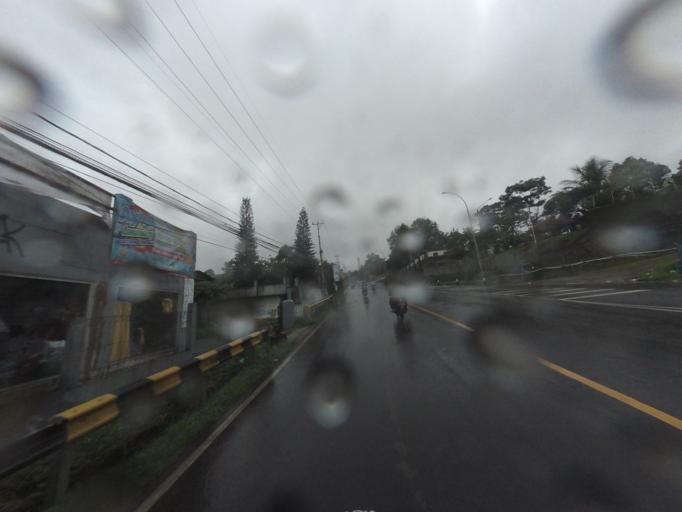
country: ID
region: West Java
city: Caringin
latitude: -6.6533
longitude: 106.8723
